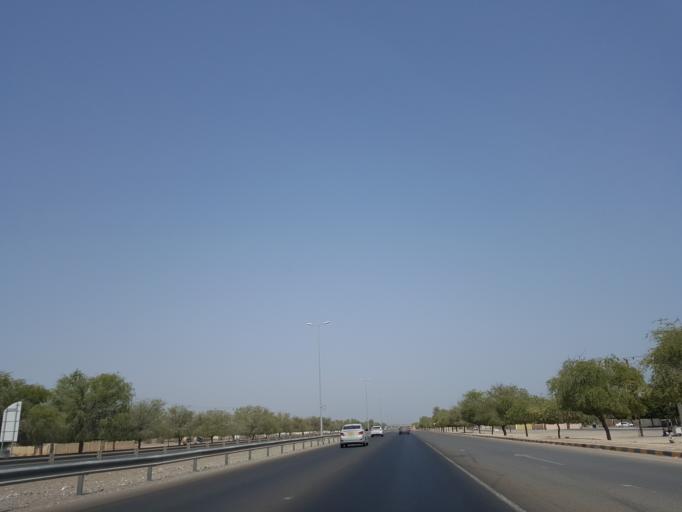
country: OM
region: Al Batinah
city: Saham
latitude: 24.0592
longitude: 56.9645
